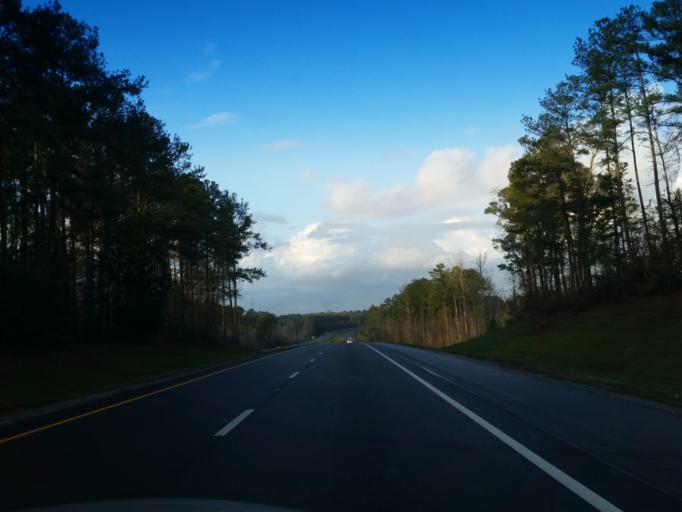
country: US
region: Mississippi
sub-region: Jones County
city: Sharon
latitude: 31.8606
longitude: -89.0468
